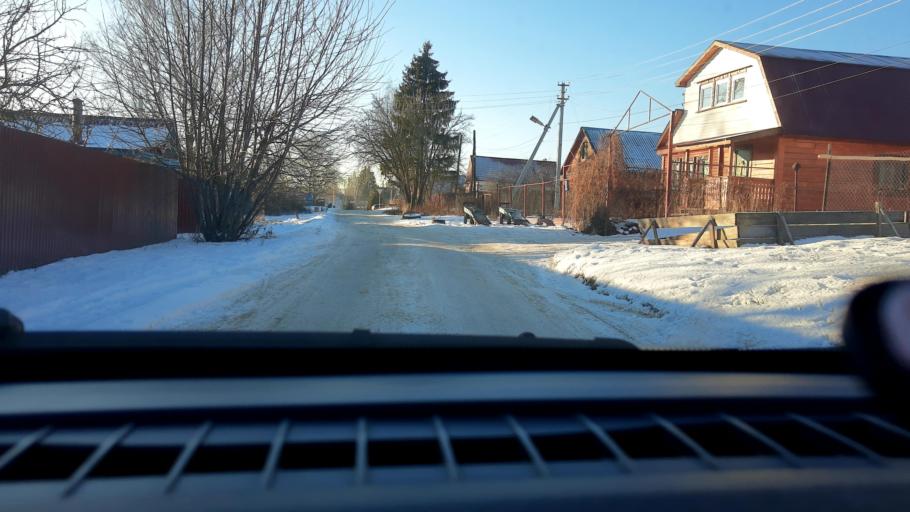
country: RU
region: Nizjnij Novgorod
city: Kstovo
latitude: 56.0403
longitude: 44.1603
